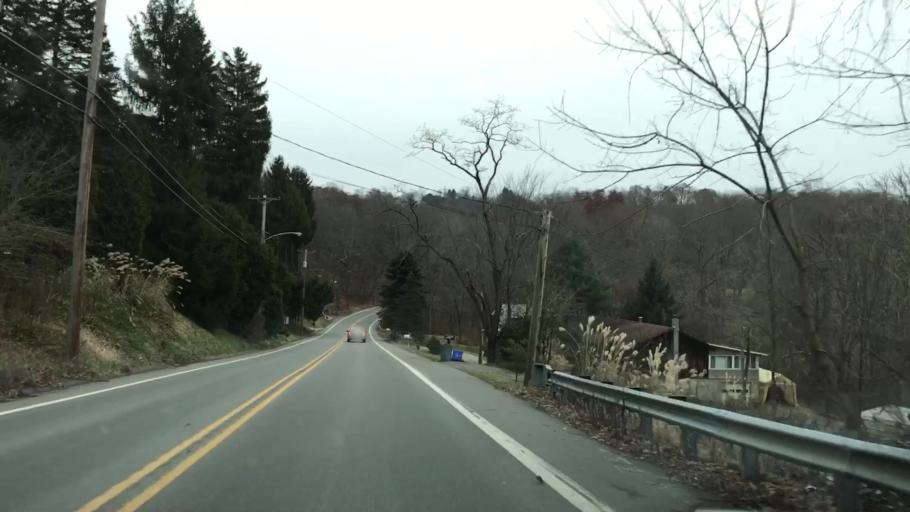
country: US
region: Pennsylvania
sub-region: Beaver County
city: Baden
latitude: 40.6424
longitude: -80.2138
